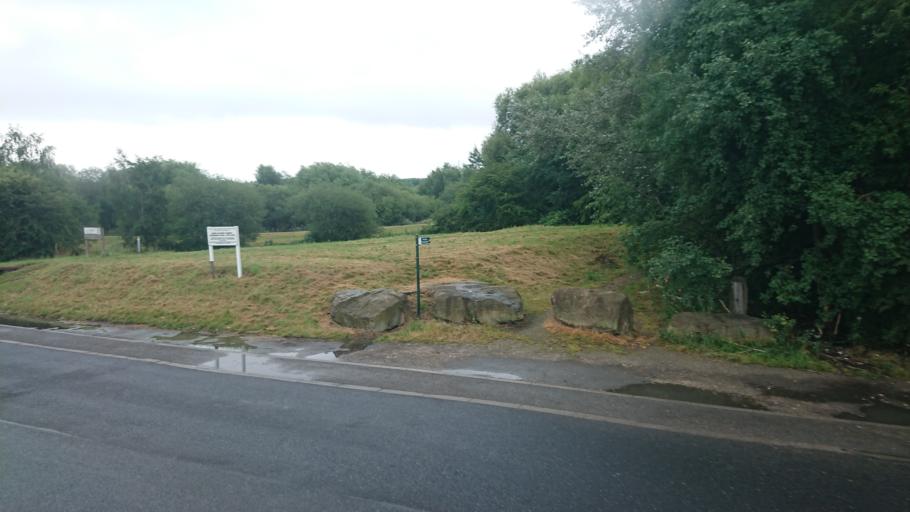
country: GB
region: England
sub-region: Rotherham
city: Orgreave
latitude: 53.3880
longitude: -1.3652
